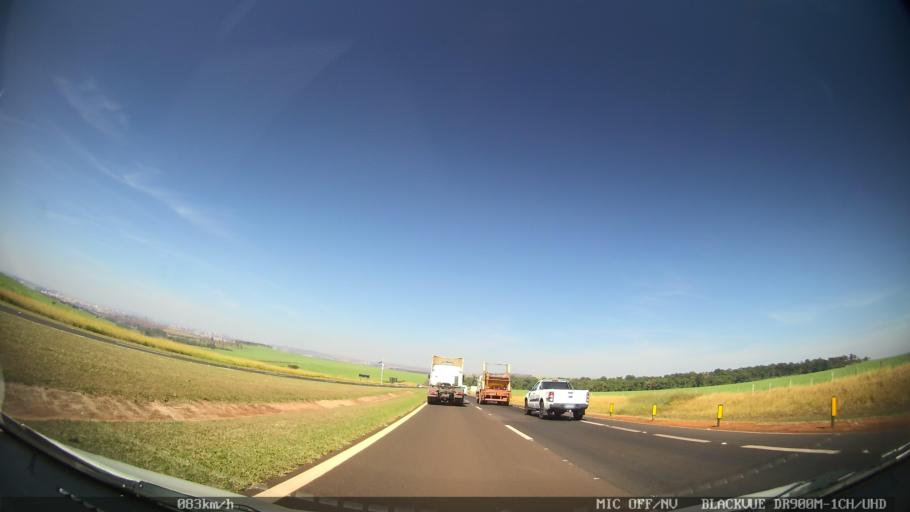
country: BR
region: Sao Paulo
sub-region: Ribeirao Preto
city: Ribeirao Preto
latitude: -21.1696
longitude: -47.8992
